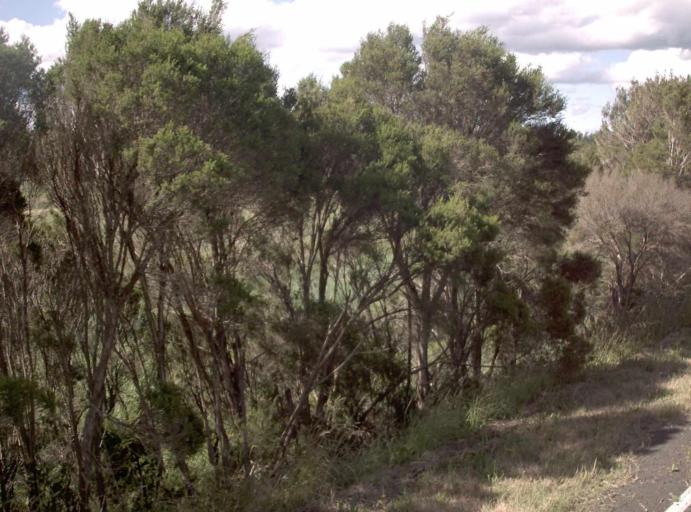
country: AU
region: Victoria
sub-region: Latrobe
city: Morwell
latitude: -38.1709
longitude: 146.4080
